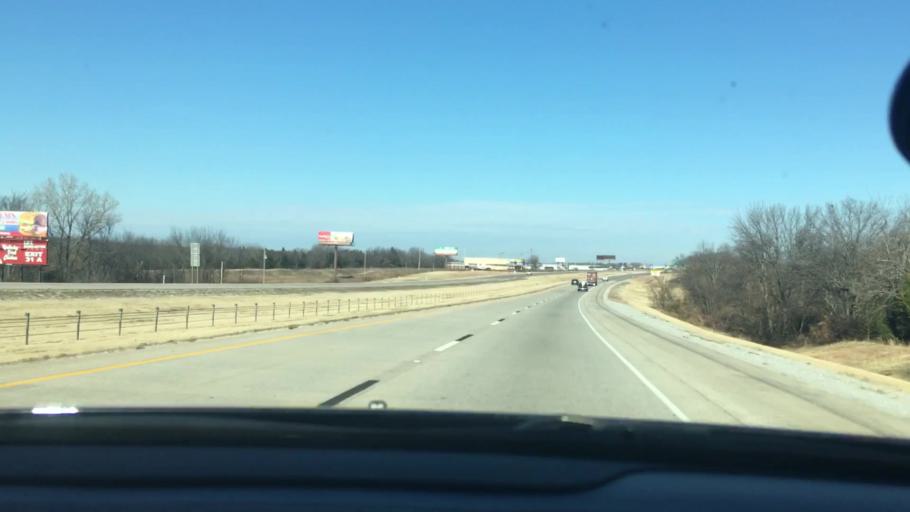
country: US
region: Oklahoma
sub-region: Carter County
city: Ardmore
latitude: 34.1608
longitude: -97.1647
